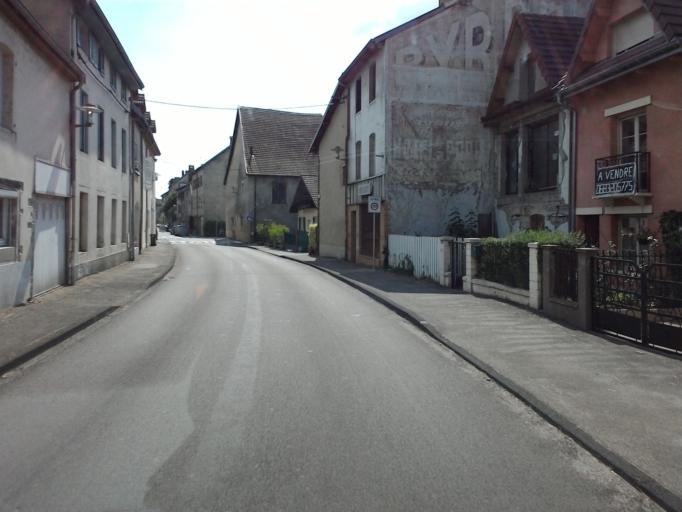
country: FR
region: Franche-Comte
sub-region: Departement du Doubs
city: Quingey
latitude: 47.1045
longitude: 5.8853
